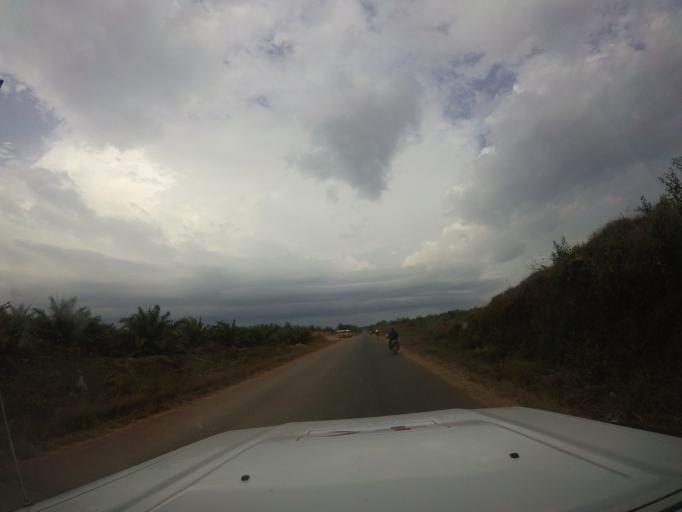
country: LR
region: Bomi
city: Tubmanburg
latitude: 6.7124
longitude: -10.9622
